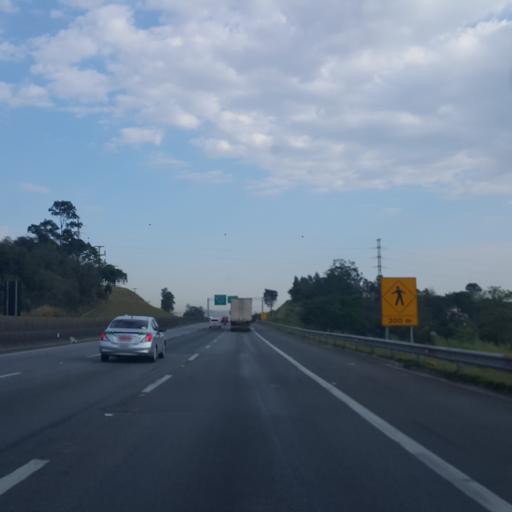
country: BR
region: Sao Paulo
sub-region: Louveira
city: Louveira
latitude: -23.0710
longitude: -46.9865
